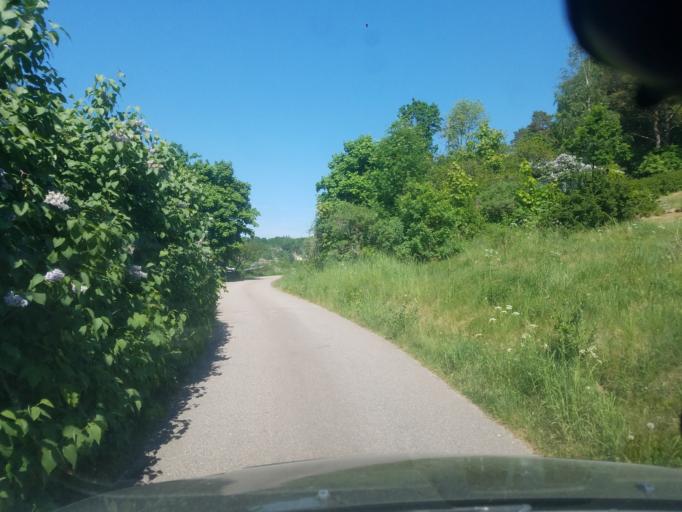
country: SE
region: Vaestra Goetaland
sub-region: Orust
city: Henan
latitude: 58.2633
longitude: 11.5721
